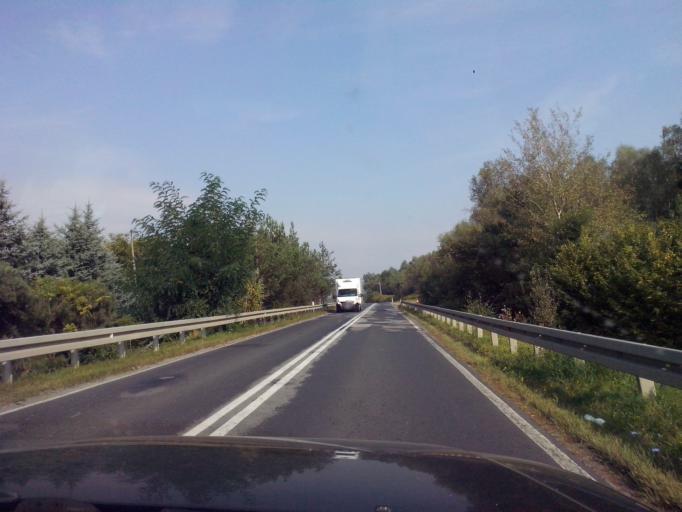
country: PL
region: Subcarpathian Voivodeship
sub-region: Powiat strzyzowski
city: Czudec
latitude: 49.9289
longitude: 21.8170
